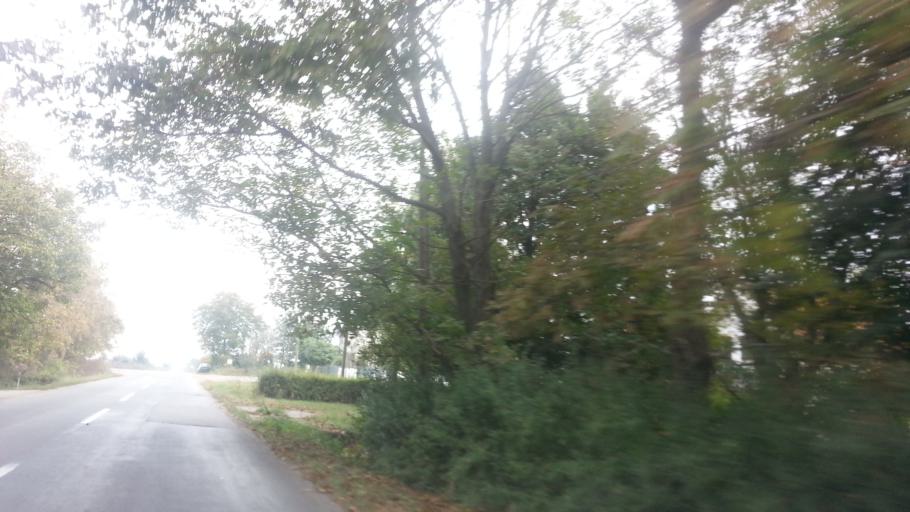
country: RS
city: Belegis
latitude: 45.0271
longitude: 20.3350
